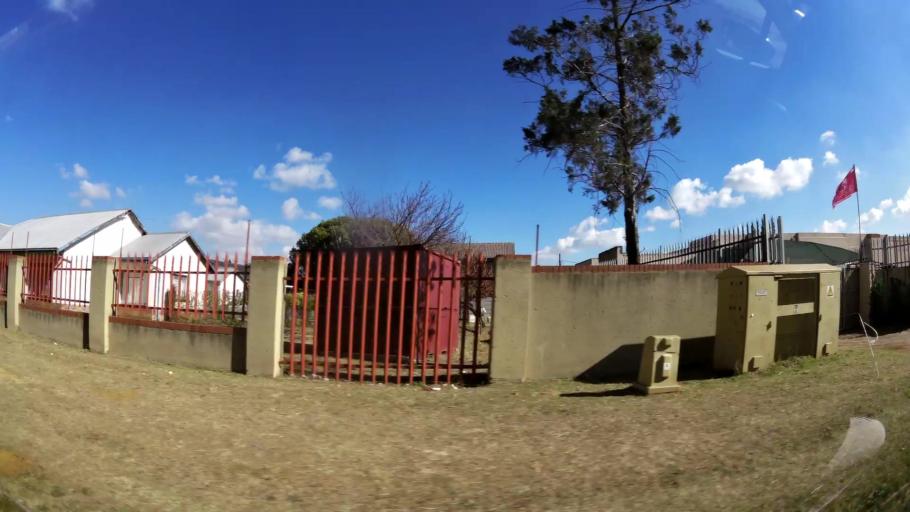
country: ZA
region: Gauteng
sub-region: City of Johannesburg Metropolitan Municipality
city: Roodepoort
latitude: -26.1344
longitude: 27.8376
